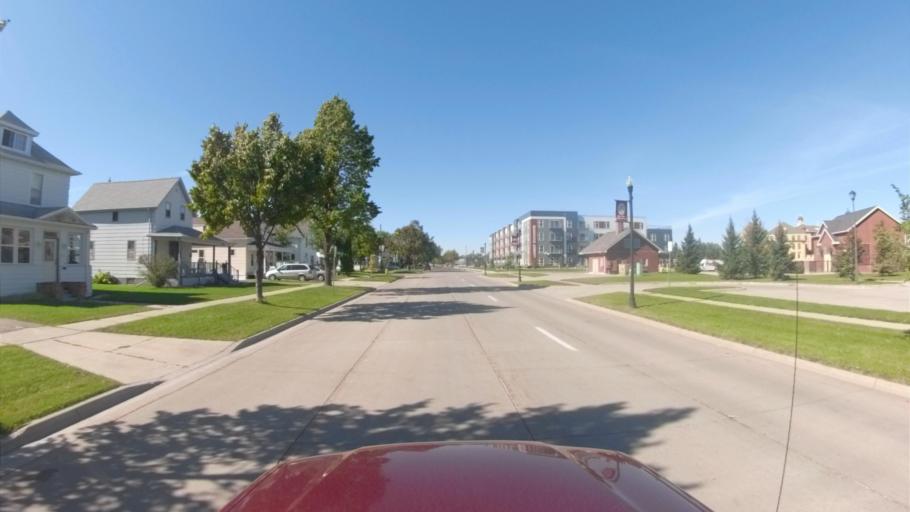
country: US
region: North Dakota
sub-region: Grand Forks County
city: Grand Forks
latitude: 47.9305
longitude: -97.0397
